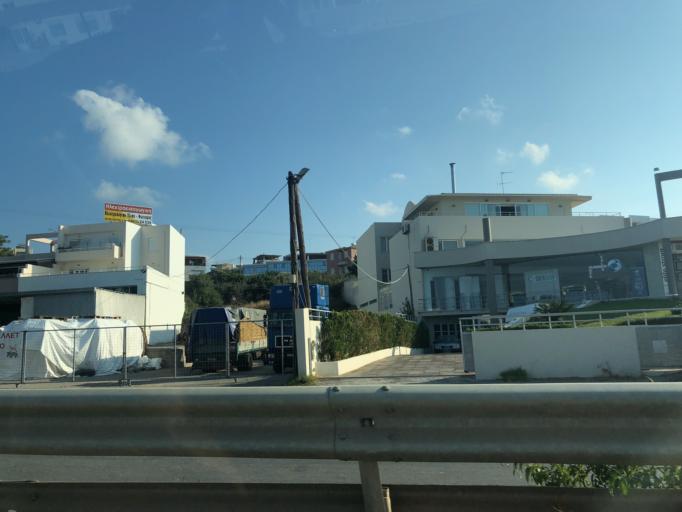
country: GR
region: Crete
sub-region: Nomos Rethymnis
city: Atsipopoulon
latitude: 35.3633
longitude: 24.4423
